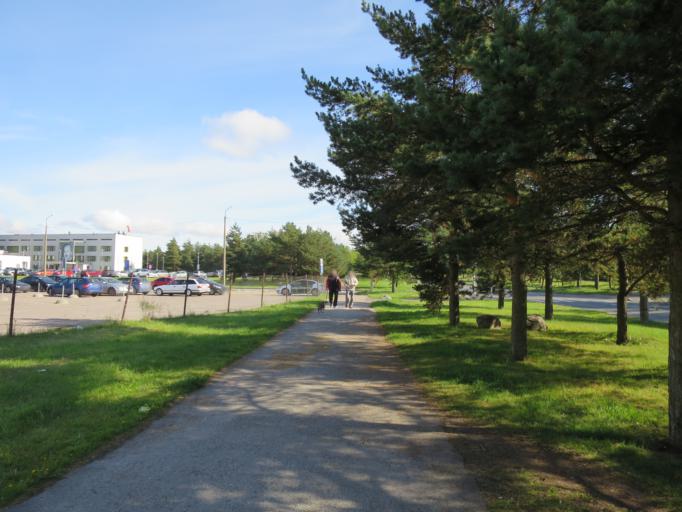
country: EE
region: Harju
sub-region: Tallinna linn
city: Tallinn
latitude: 59.3970
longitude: 24.6993
